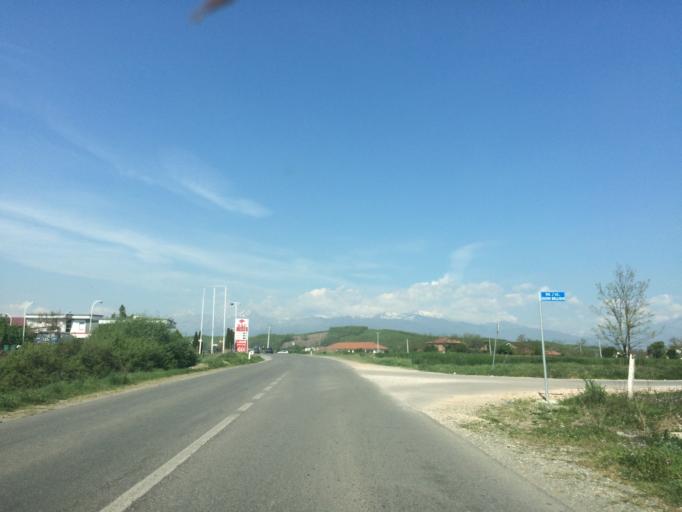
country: XK
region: Gjakova
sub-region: Komuna e Gjakoves
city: Gjakove
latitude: 42.3743
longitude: 20.4004
